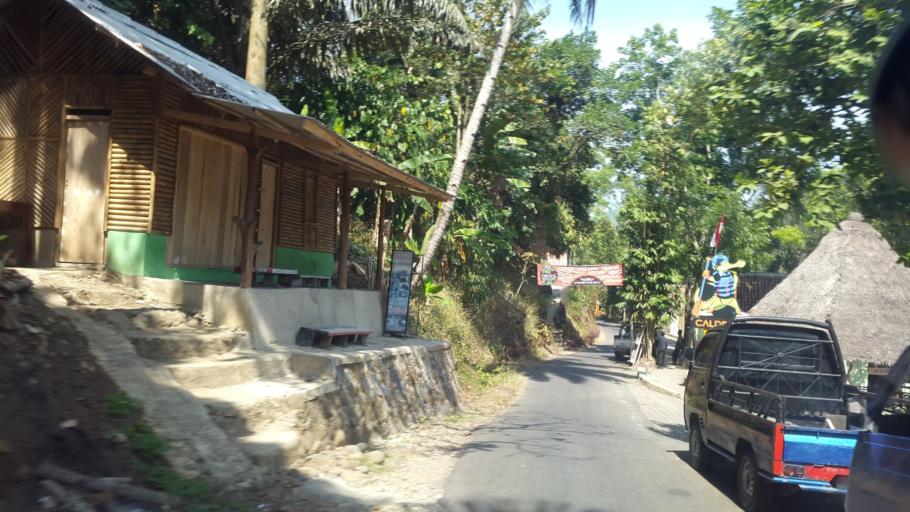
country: ID
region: West Java
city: Bojonggaling
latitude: -6.9153
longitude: 106.6119
